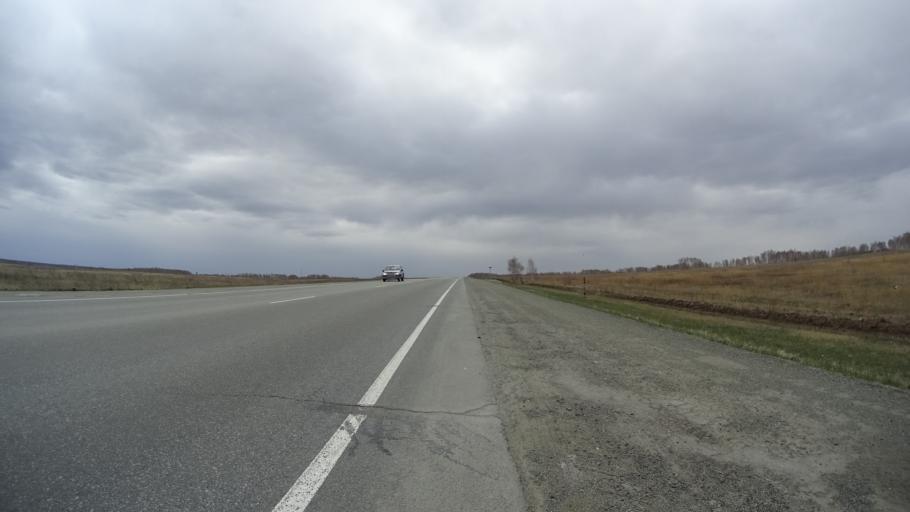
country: RU
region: Chelyabinsk
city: Yemanzhelinsk
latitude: 54.7075
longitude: 61.2577
